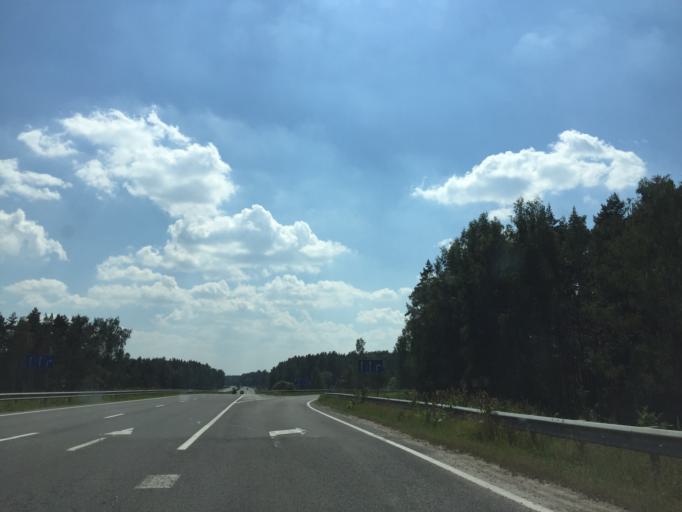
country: LV
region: Babite
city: Pinki
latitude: 56.9527
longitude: 23.9274
